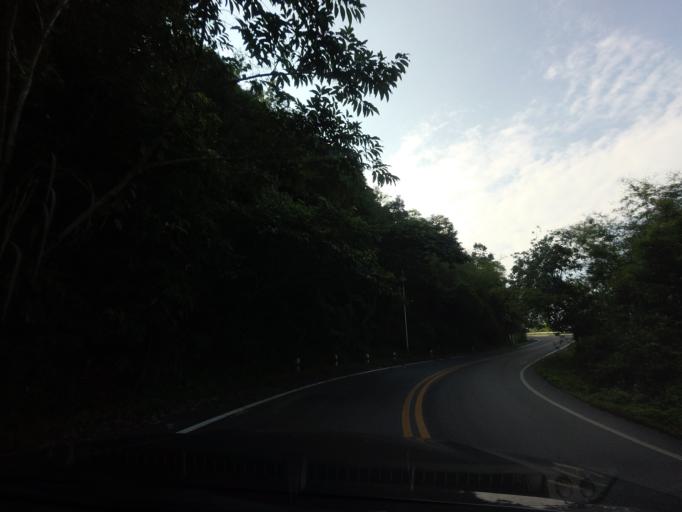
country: TH
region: Nan
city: Na Noi
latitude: 18.3684
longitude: 100.8320
